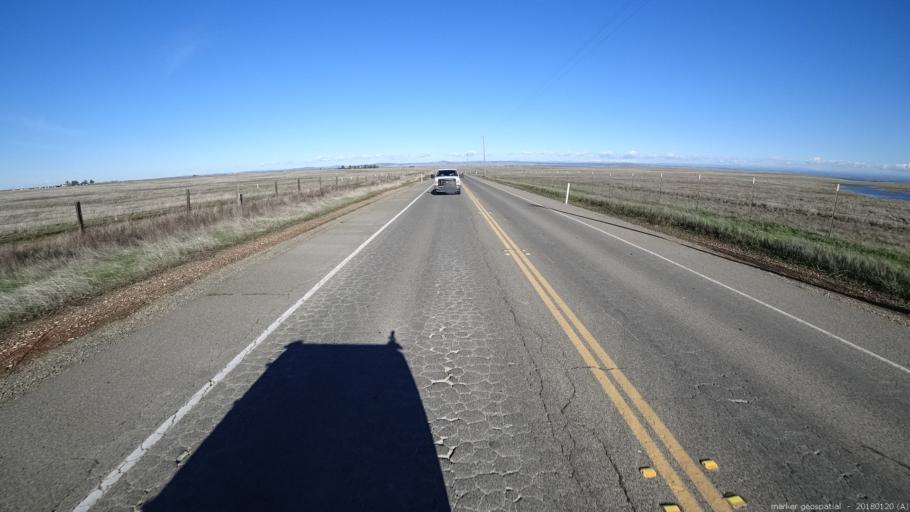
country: US
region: California
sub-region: Sacramento County
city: Rancho Murieta
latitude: 38.5314
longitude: -121.1904
